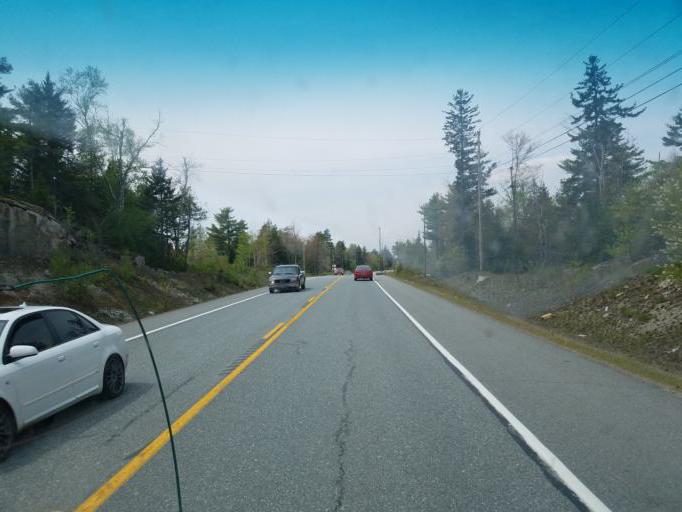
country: US
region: Maine
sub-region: Hancock County
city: Ellsworth
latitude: 44.5833
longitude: -68.4883
